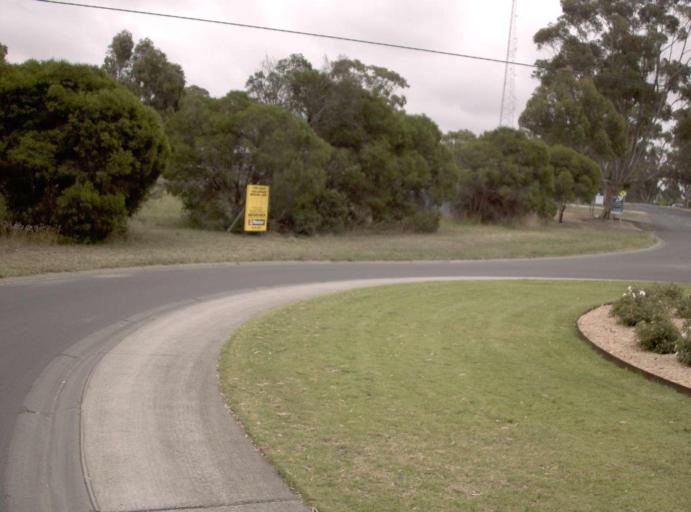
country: AU
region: Victoria
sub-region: Wellington
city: Heyfield
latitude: -37.9787
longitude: 146.7843
